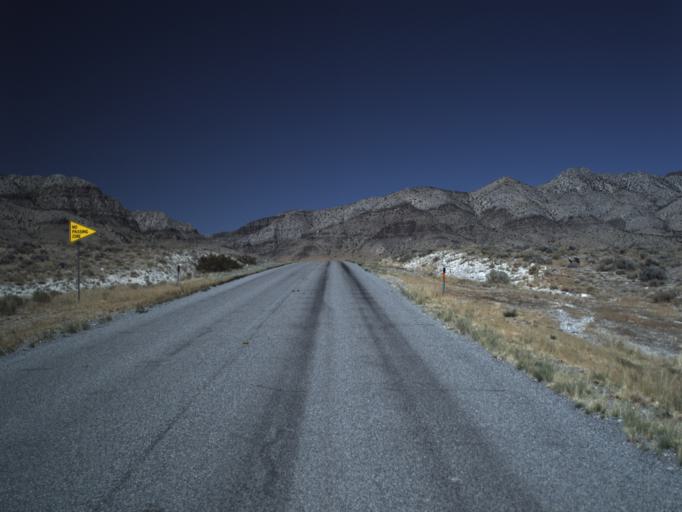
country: US
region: Utah
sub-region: Beaver County
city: Milford
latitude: 39.0859
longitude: -113.5260
